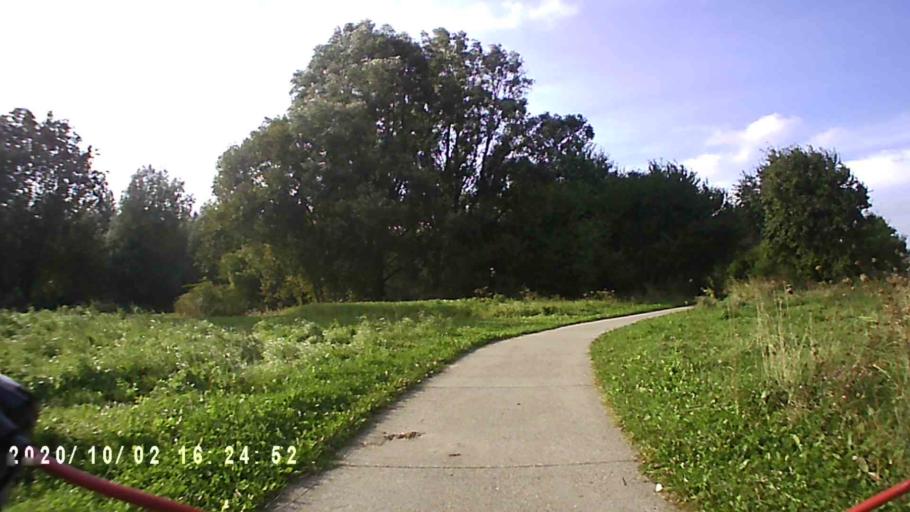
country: NL
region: Groningen
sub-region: Gemeente Zuidhorn
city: Grijpskerk
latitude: 53.2816
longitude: 6.3151
